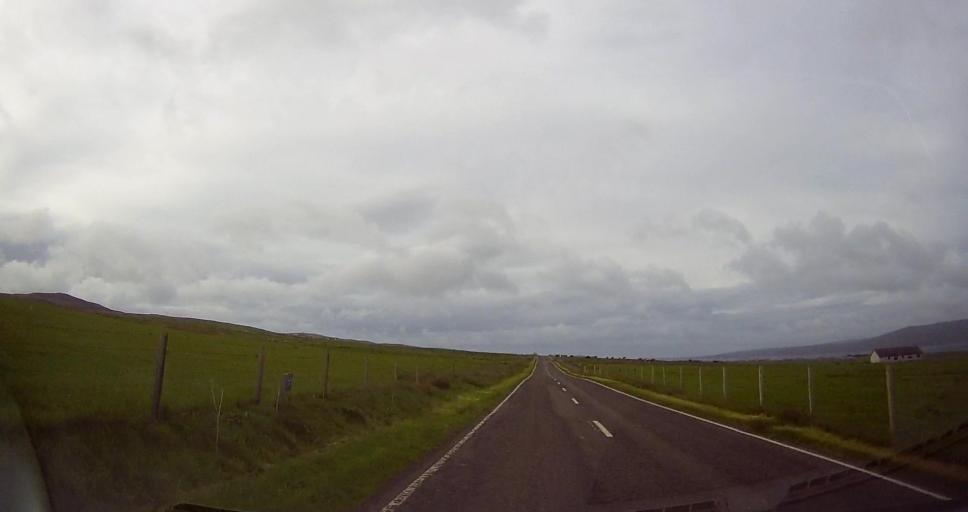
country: GB
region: Scotland
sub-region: Orkney Islands
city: Stromness
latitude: 58.9502
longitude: -3.2168
